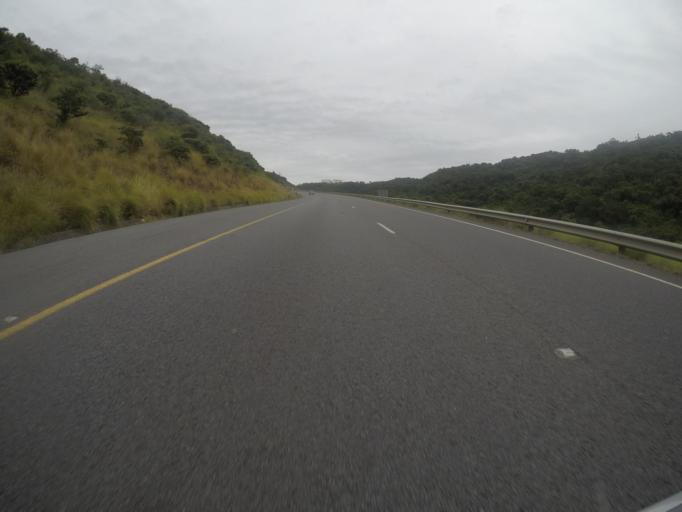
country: ZA
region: Eastern Cape
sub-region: Buffalo City Metropolitan Municipality
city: East London
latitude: -32.9689
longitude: 27.9137
